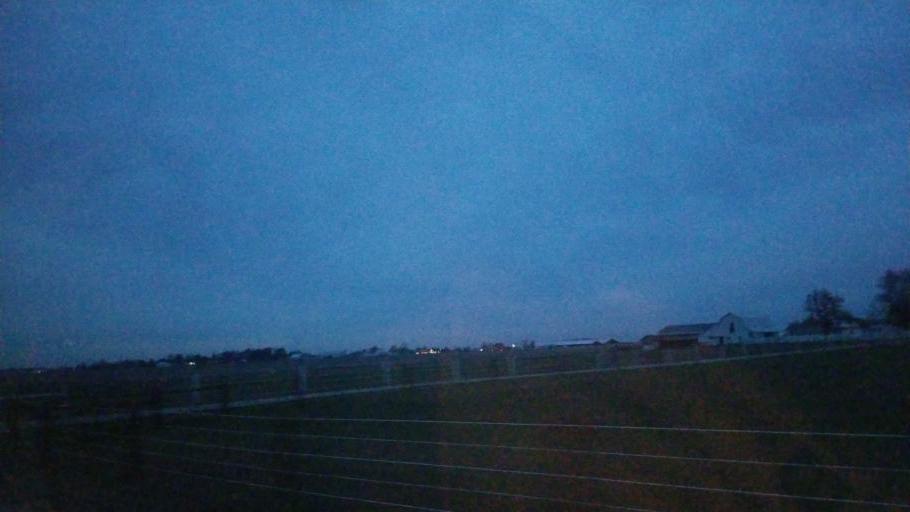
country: US
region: Indiana
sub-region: Adams County
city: Berne
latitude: 40.6940
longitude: -84.9641
